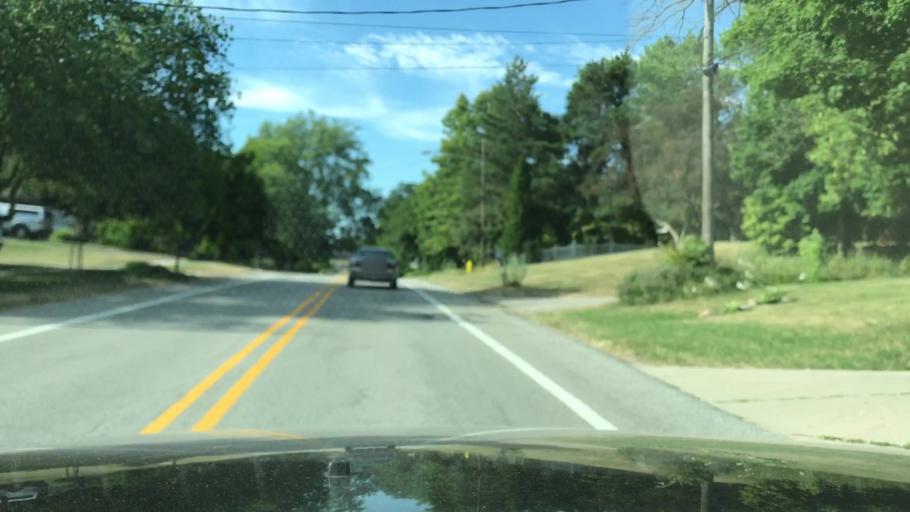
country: US
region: Michigan
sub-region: Kent County
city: East Grand Rapids
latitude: 42.9815
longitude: -85.6104
